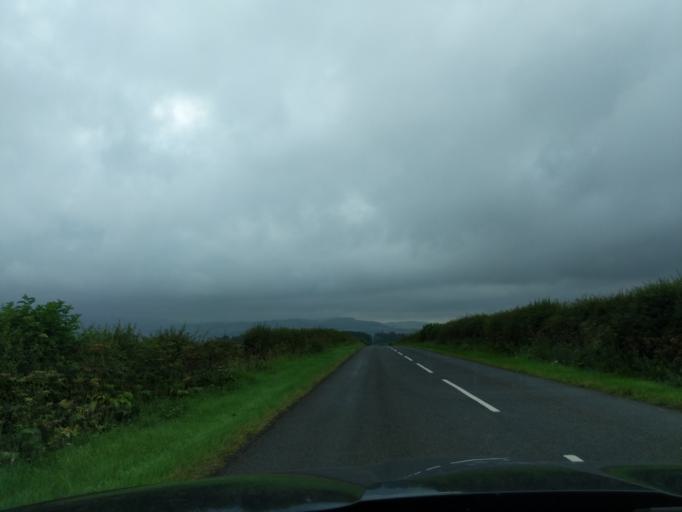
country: GB
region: England
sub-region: Northumberland
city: Ford
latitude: 55.6404
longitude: -2.0648
